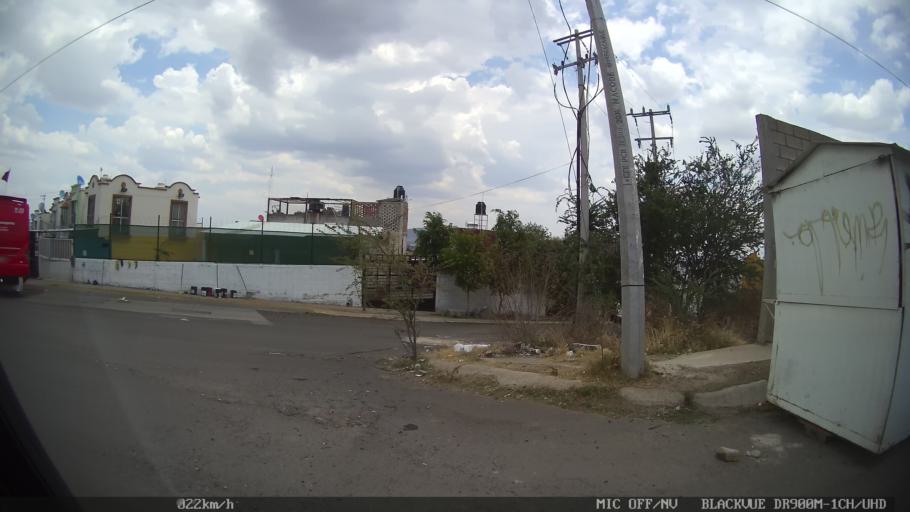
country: MX
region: Jalisco
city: Tonala
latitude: 20.6401
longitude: -103.2290
